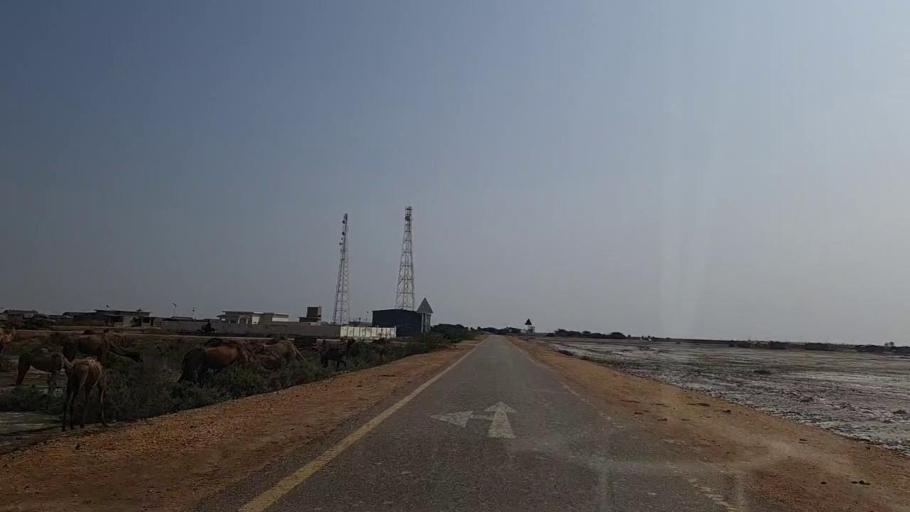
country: PK
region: Sindh
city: Chuhar Jamali
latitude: 24.1663
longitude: 67.8984
